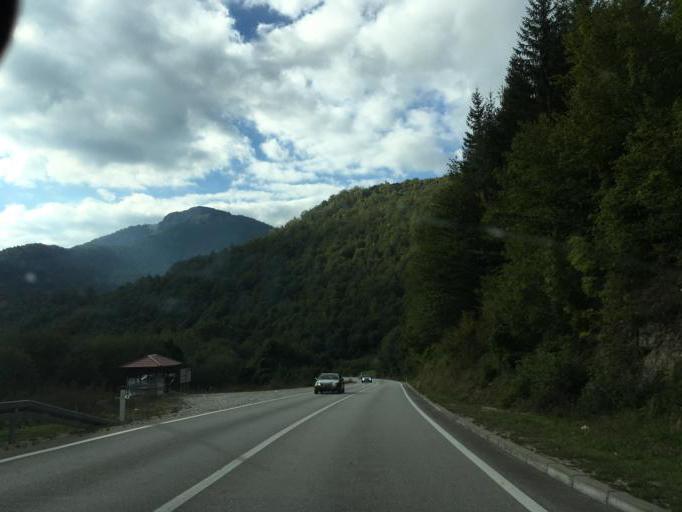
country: BA
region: Federation of Bosnia and Herzegovina
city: Bugojno
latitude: 44.0930
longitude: 17.5654
